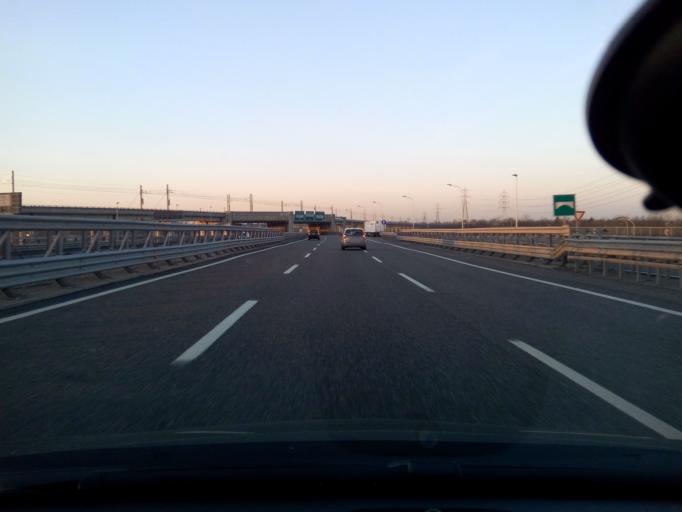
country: IT
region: Lombardy
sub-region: Citta metropolitana di Milano
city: Rho
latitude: 45.5224
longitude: 9.0597
